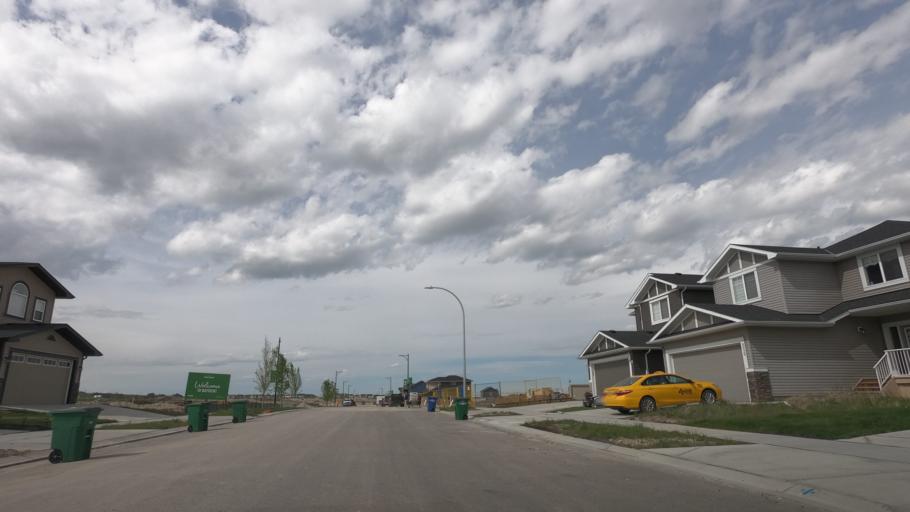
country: CA
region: Alberta
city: Airdrie
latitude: 51.2780
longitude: -114.0437
